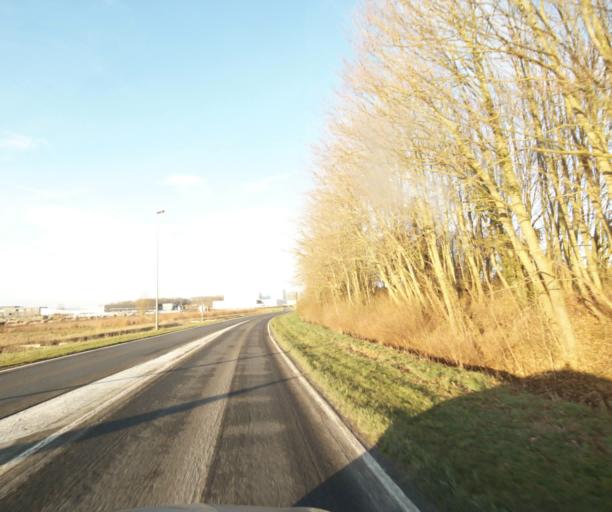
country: FR
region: Nord-Pas-de-Calais
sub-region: Departement du Nord
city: Famars
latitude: 50.3153
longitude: 3.5131
